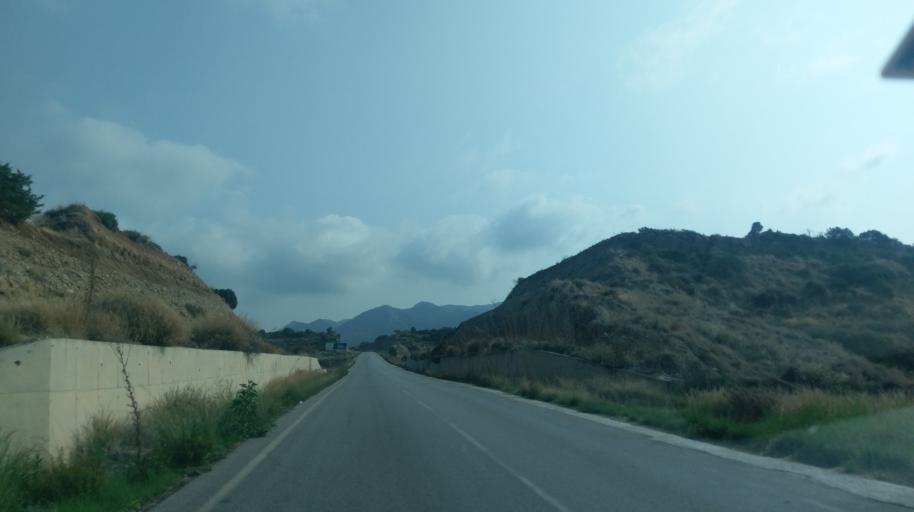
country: CY
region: Ammochostos
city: Lefkonoiko
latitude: 35.3538
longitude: 33.6194
